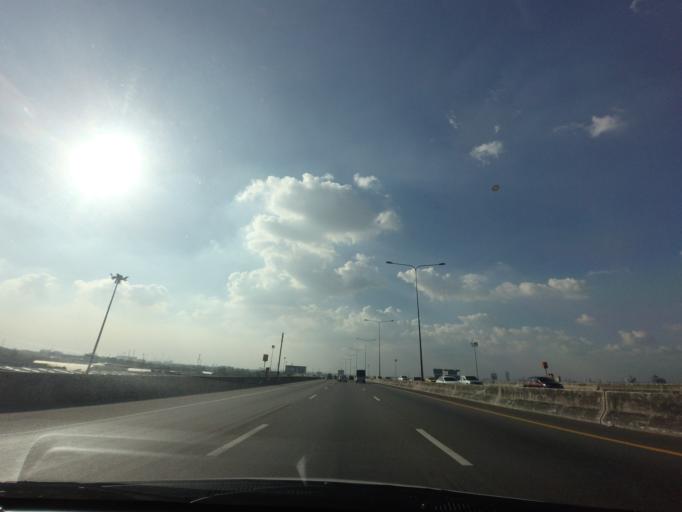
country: TH
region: Samut Prakan
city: Phra Samut Chedi
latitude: 13.6302
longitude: 100.5876
